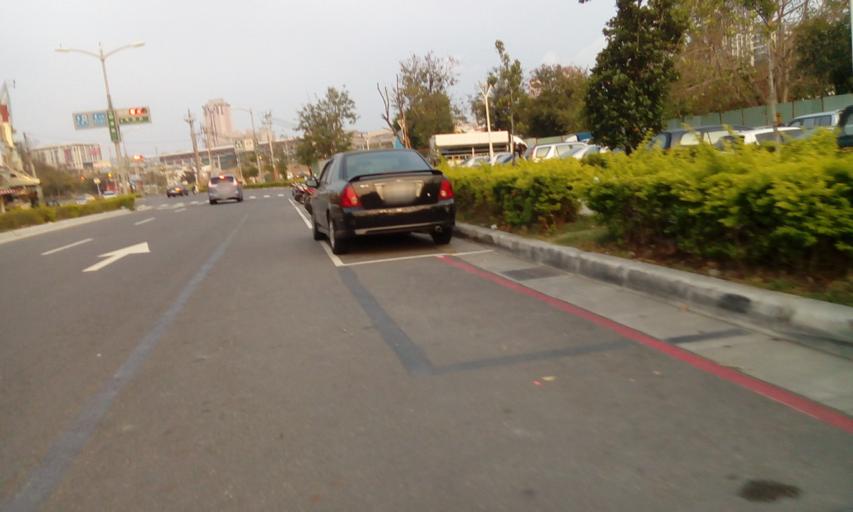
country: TW
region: Kaohsiung
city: Kaohsiung
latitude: 22.6890
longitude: 120.3009
